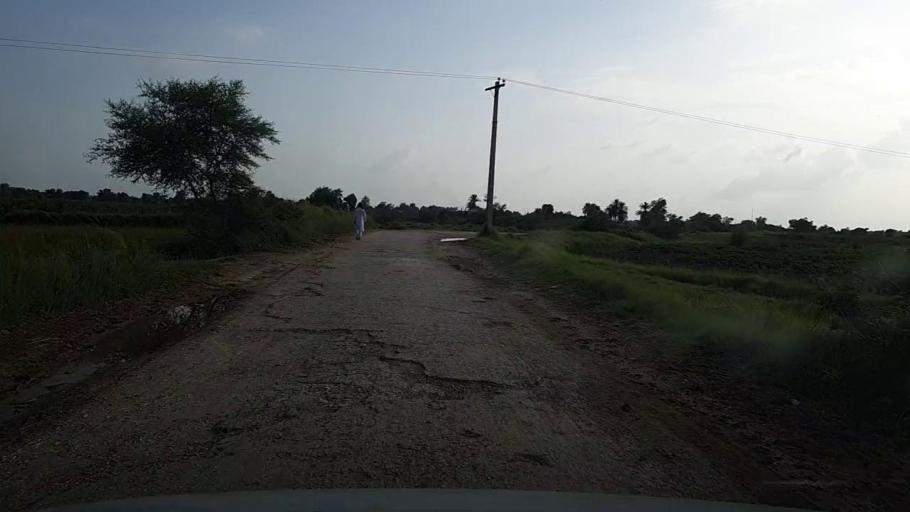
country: PK
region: Sindh
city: Pad Idan
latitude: 26.7957
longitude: 68.2330
